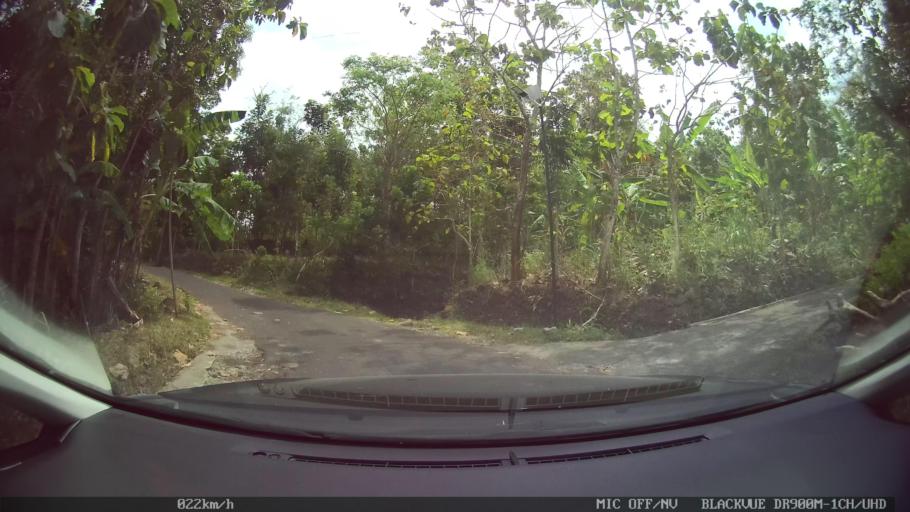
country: ID
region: Central Java
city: Candi Prambanan
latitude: -7.8060
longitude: 110.5219
